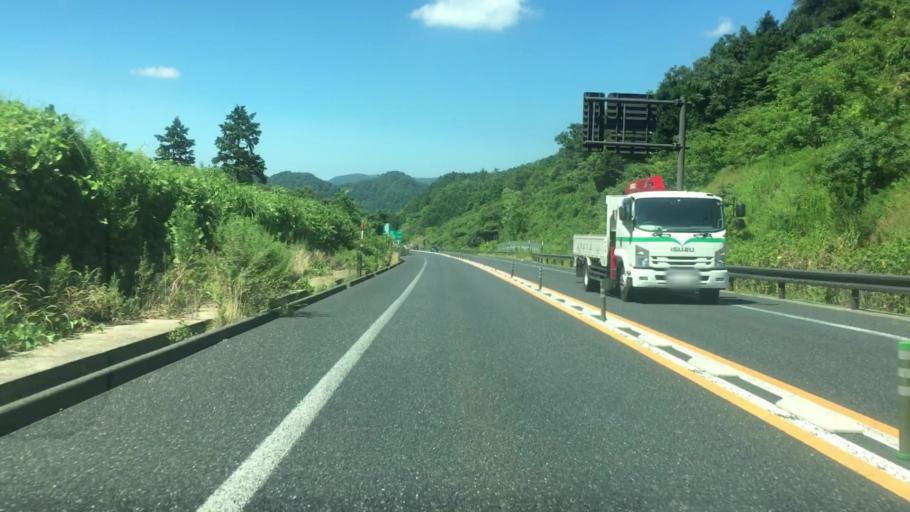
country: JP
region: Tottori
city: Tottori
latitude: 35.3639
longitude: 134.2016
